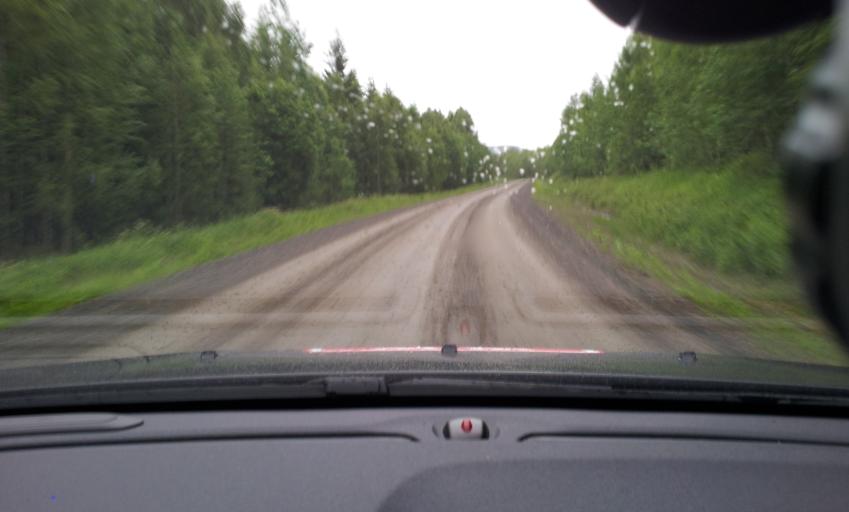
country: SE
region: Jaemtland
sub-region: Ragunda Kommun
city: Hammarstrand
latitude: 63.1399
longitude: 16.2723
